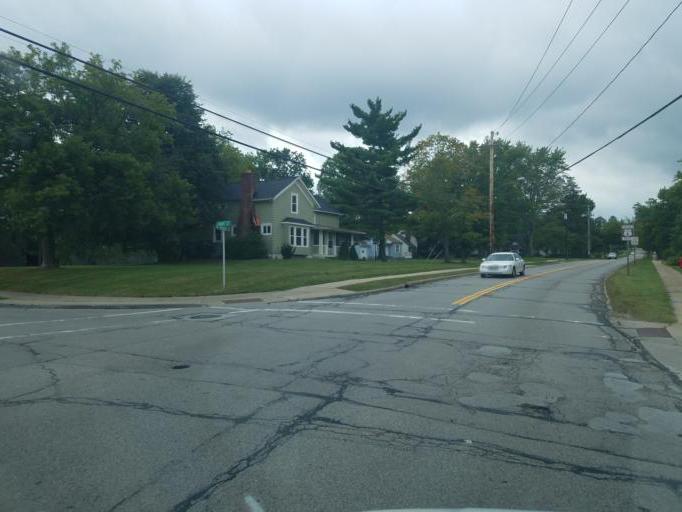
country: US
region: Ohio
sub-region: Geauga County
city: Chardon
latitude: 41.5837
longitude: -81.1910
